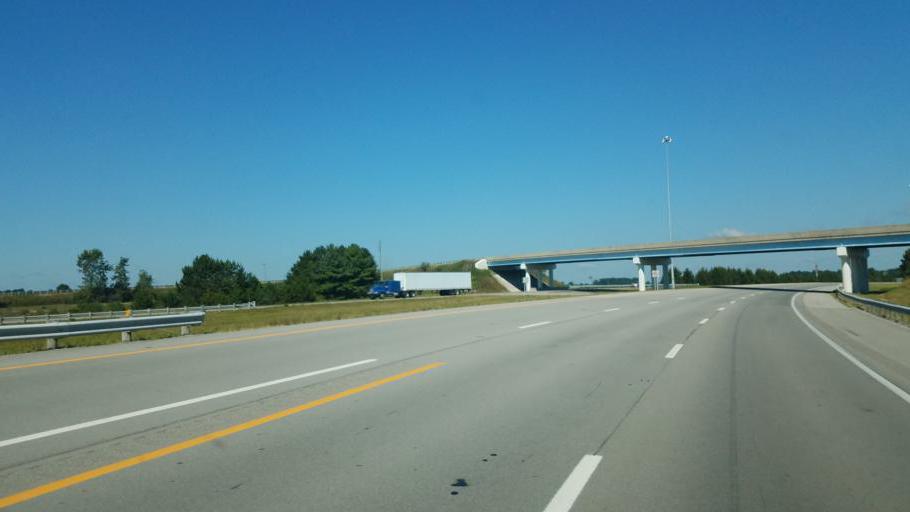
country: US
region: Ohio
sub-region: Wyandot County
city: Upper Sandusky
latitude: 40.8608
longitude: -83.3213
